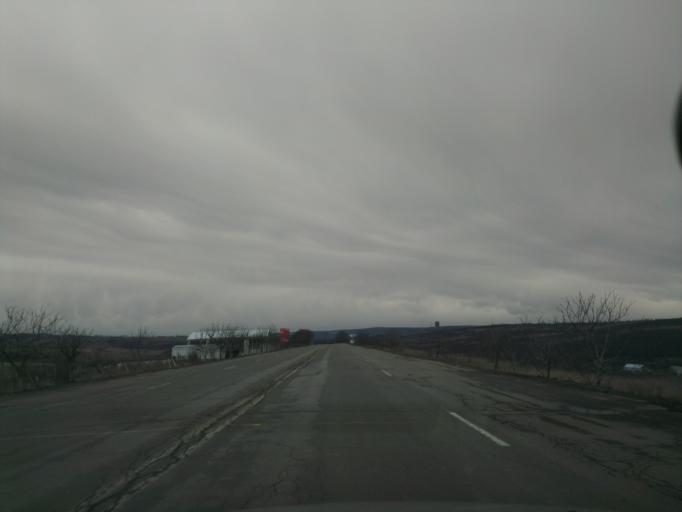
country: MD
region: Chisinau
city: Vatra
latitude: 47.0023
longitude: 28.7310
